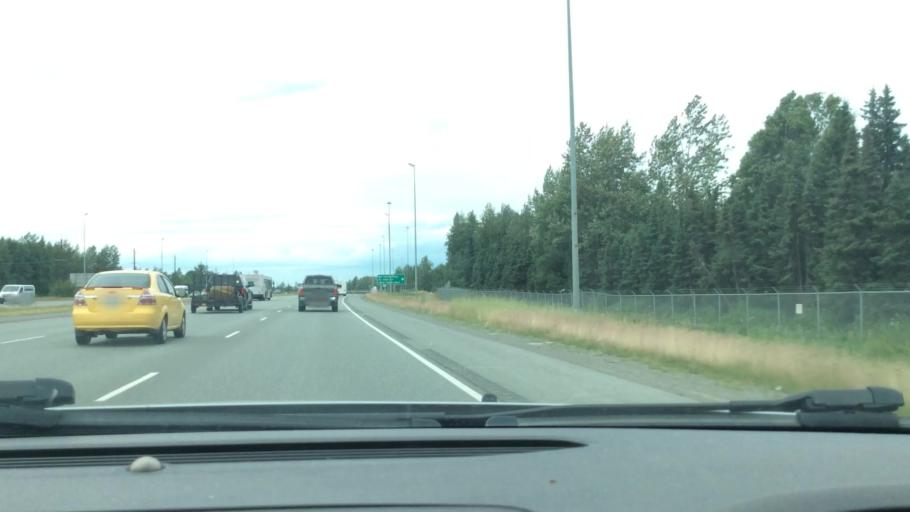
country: US
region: Alaska
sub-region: Anchorage Municipality
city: Anchorage
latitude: 61.2247
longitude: -149.7642
